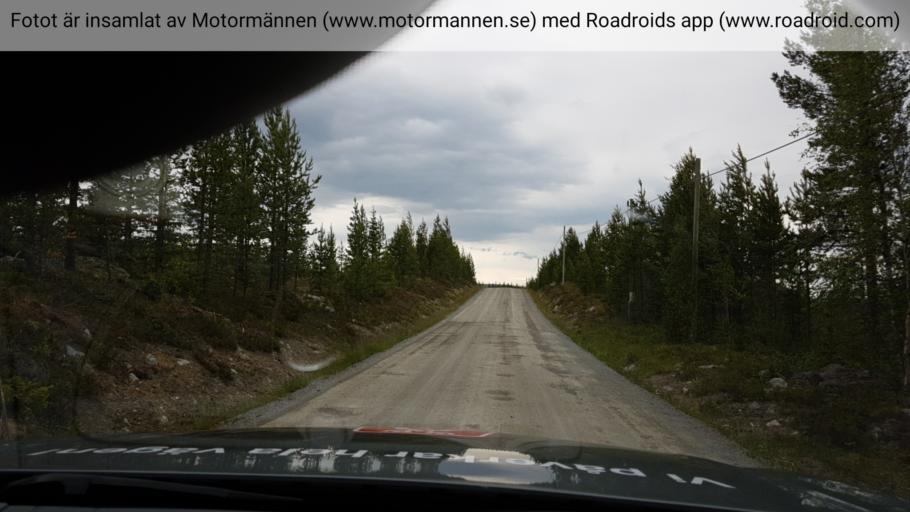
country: SE
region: Jaemtland
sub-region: Are Kommun
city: Jarpen
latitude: 62.8009
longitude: 13.8021
